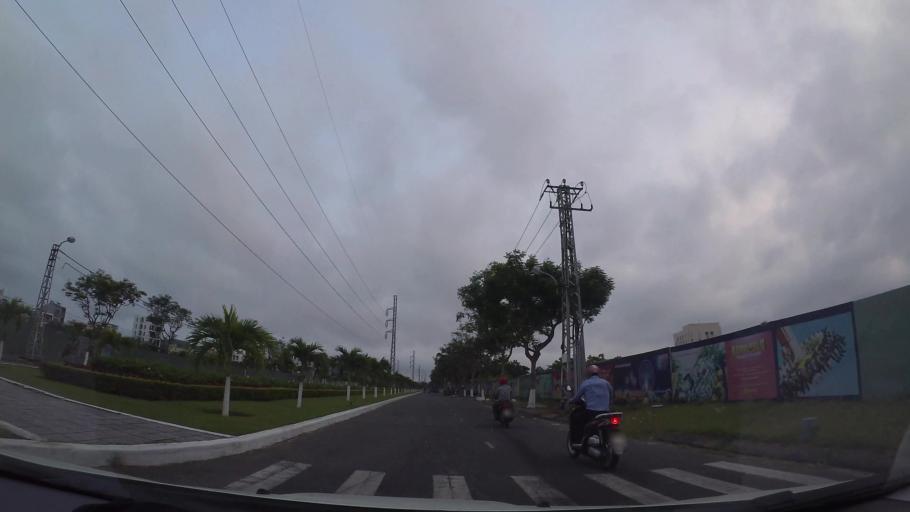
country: VN
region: Da Nang
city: Son Tra
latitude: 16.0435
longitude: 108.2374
